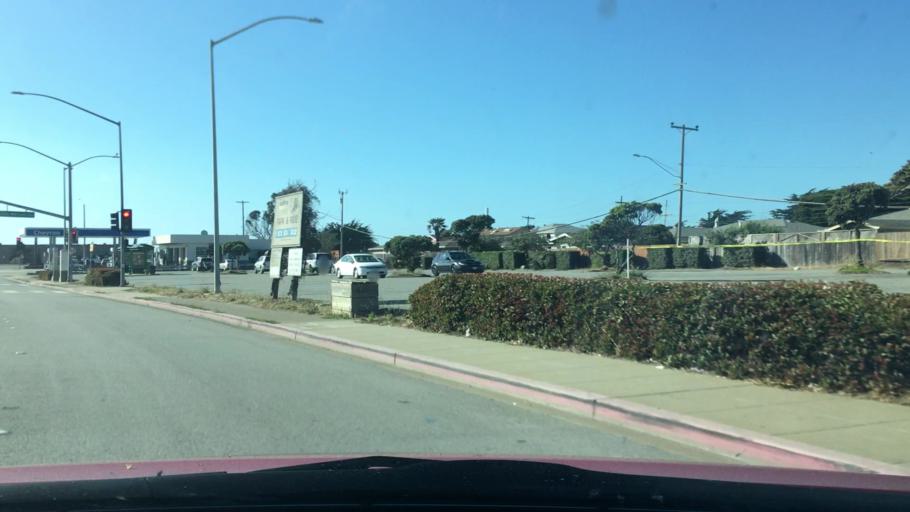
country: US
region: California
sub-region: San Mateo County
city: Pacifica
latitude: 37.5949
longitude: -122.5023
